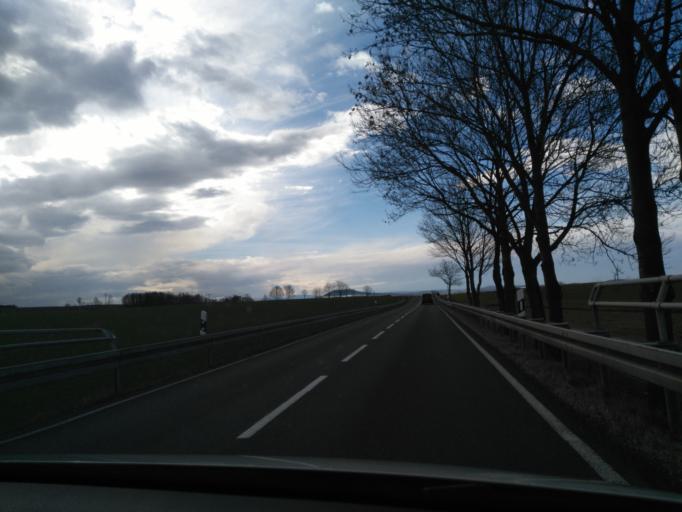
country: DE
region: Saxony
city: Wolkenstein
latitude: 50.6690
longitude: 13.1049
